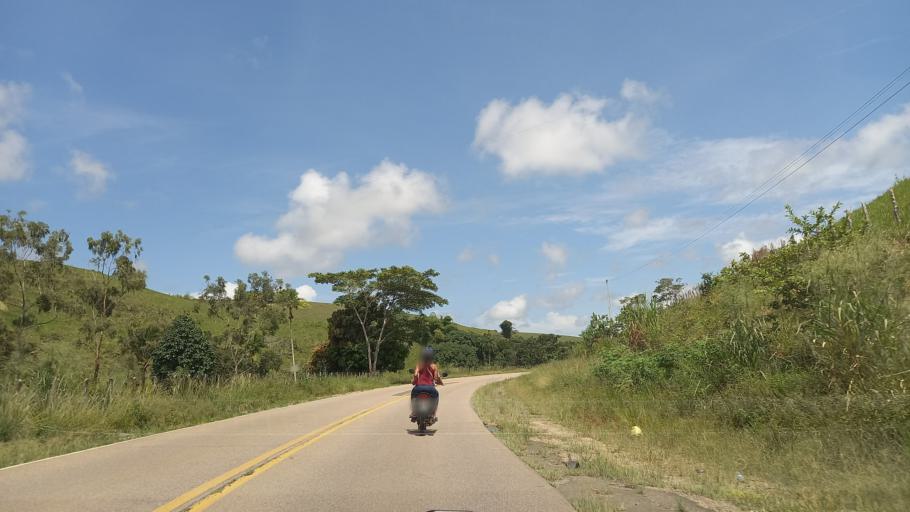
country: BR
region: Pernambuco
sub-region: Tamandare
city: Tamandare
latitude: -8.7473
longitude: -35.1711
